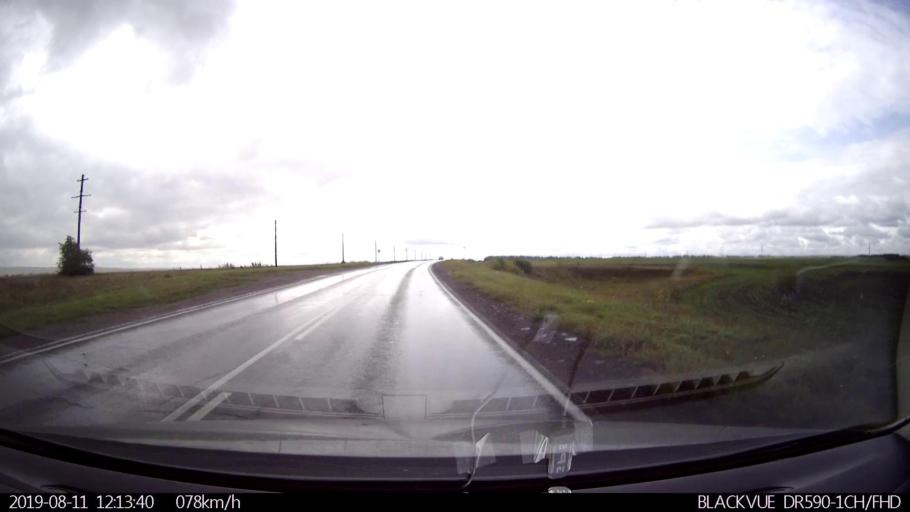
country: RU
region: Ulyanovsk
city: Ignatovka
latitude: 53.9597
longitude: 47.9900
